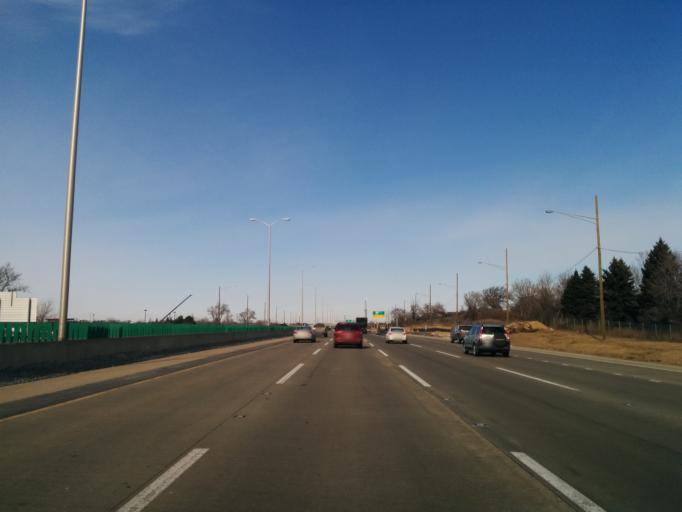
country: US
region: Illinois
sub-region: Lake County
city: Gurnee
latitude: 42.3722
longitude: -87.9430
